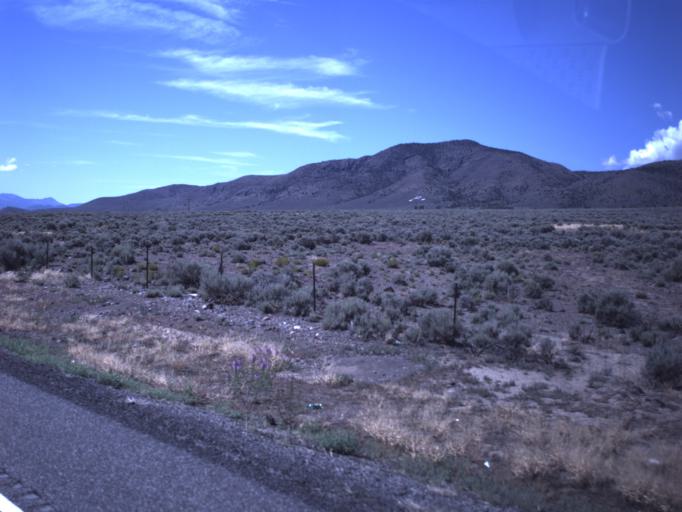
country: US
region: Utah
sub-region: Piute County
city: Junction
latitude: 38.2687
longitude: -112.2223
